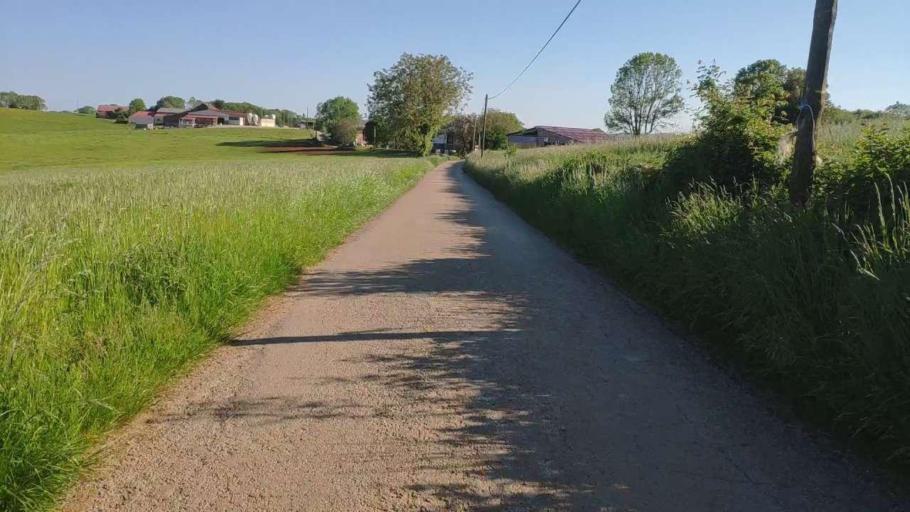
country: FR
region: Franche-Comte
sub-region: Departement du Jura
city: Perrigny
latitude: 46.7211
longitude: 5.6222
